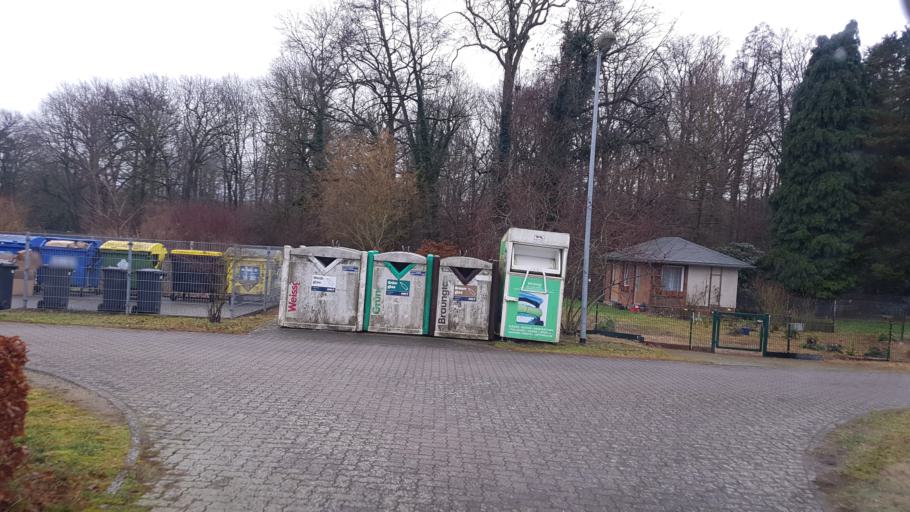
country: DE
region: Brandenburg
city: Altdobern
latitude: 51.6907
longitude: 14.0052
